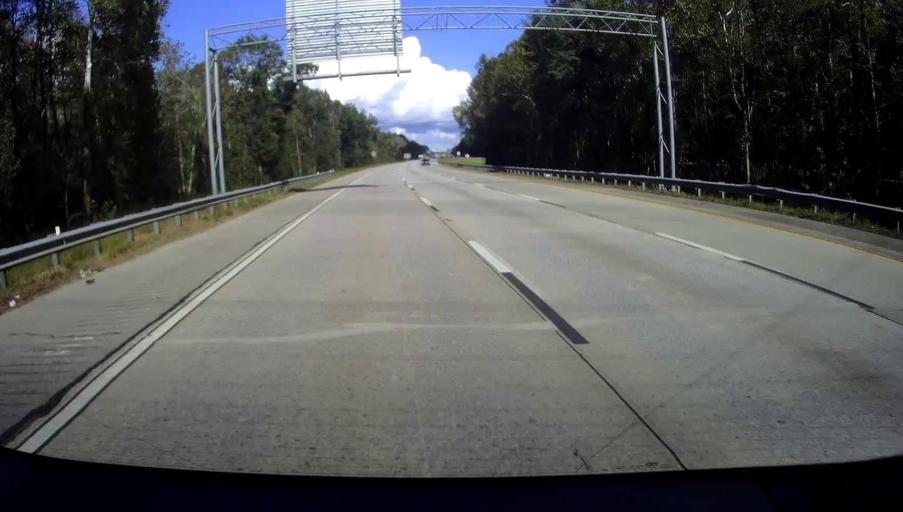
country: US
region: Georgia
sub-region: Bibb County
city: Macon
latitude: 32.7663
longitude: -83.7018
